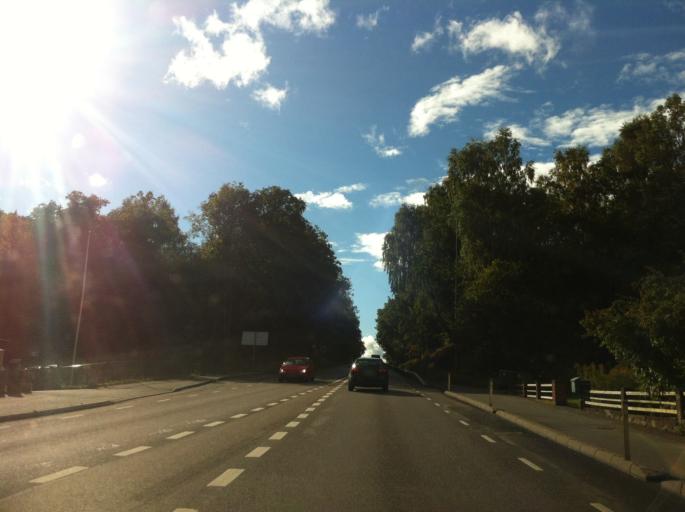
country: SE
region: Skane
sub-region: Hassleholms Kommun
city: Sosdala
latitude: 56.1636
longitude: 13.5877
